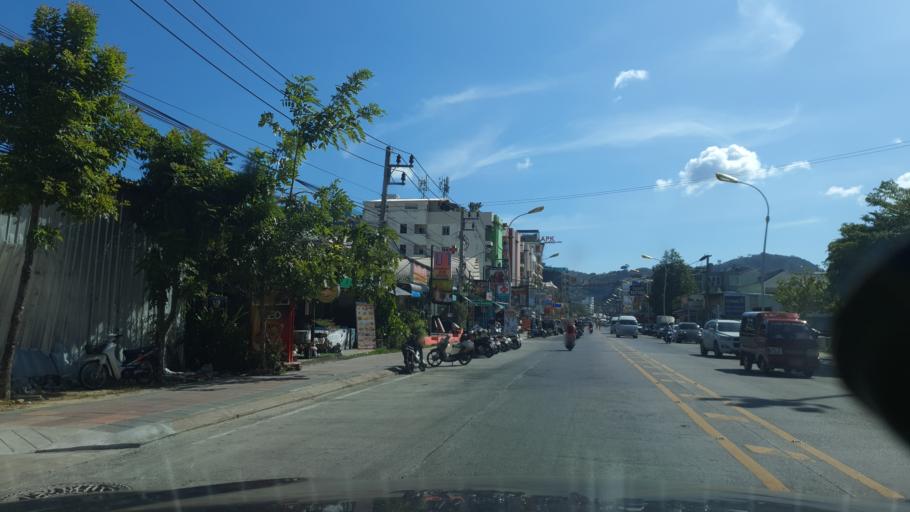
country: TH
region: Phuket
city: Patong
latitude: 7.8952
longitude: 98.3020
